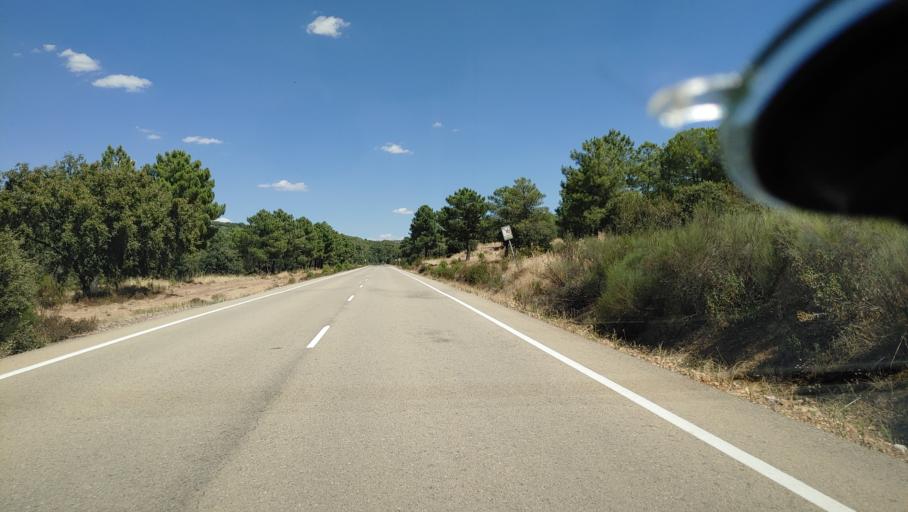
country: ES
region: Castille-La Mancha
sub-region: Provincia de Ciudad Real
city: Saceruela
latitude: 38.9890
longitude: -4.5439
